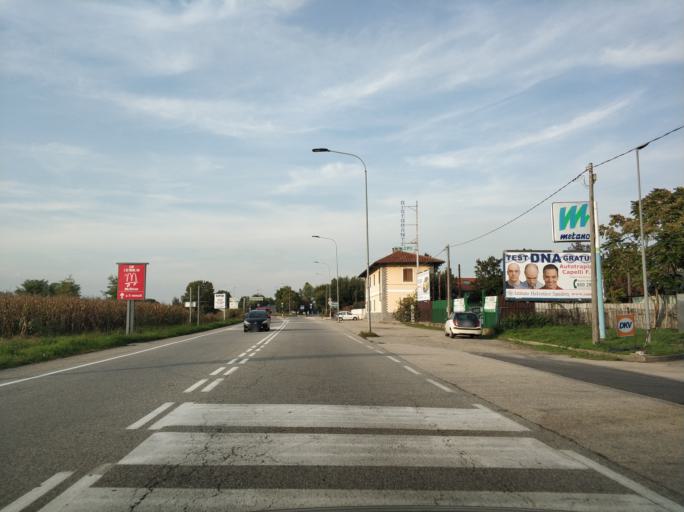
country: IT
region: Piedmont
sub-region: Provincia di Torino
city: Borgaro Torinese
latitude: 45.1262
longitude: 7.7037
